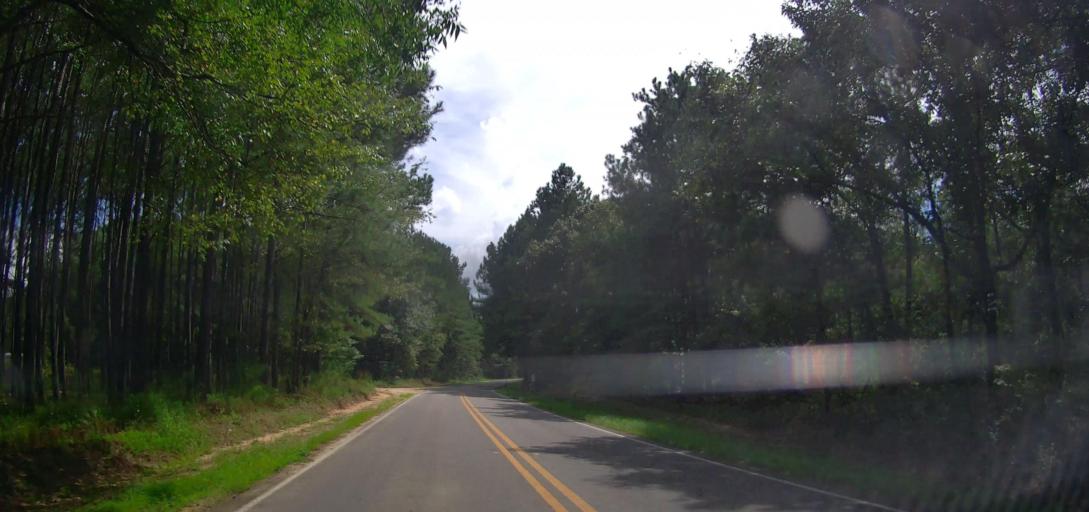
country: US
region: Georgia
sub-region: Taylor County
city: Butler
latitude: 32.5027
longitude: -84.2023
